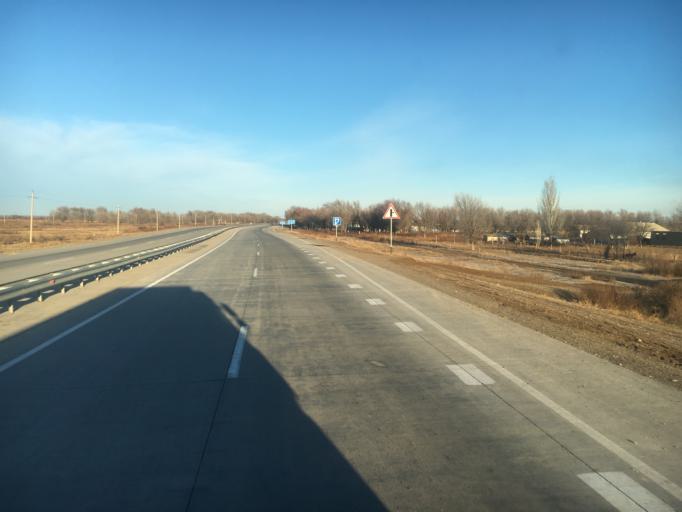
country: KZ
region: Ongtustik Qazaqstan
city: Turkestan
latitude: 43.1433
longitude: 68.5797
